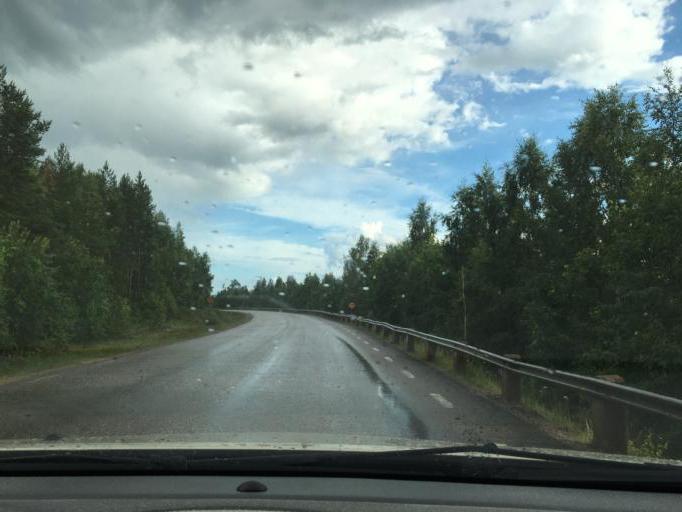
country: SE
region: Norrbotten
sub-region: Kalix Kommun
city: Rolfs
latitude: 65.9348
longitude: 22.8923
